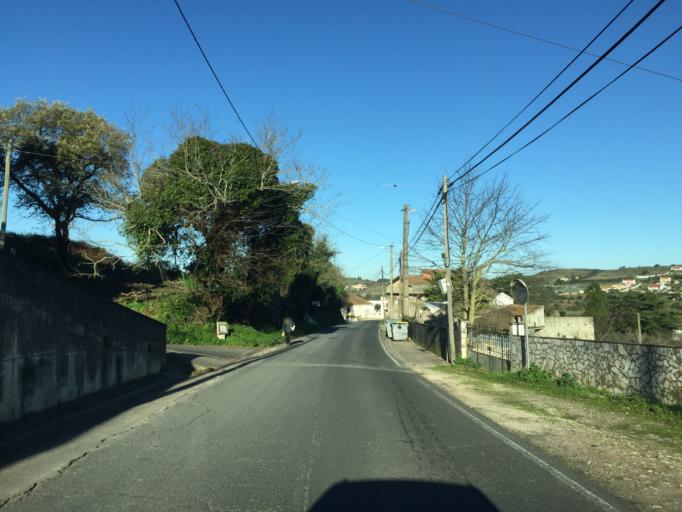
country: PT
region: Lisbon
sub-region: Odivelas
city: Canecas
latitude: 38.8232
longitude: -9.2355
